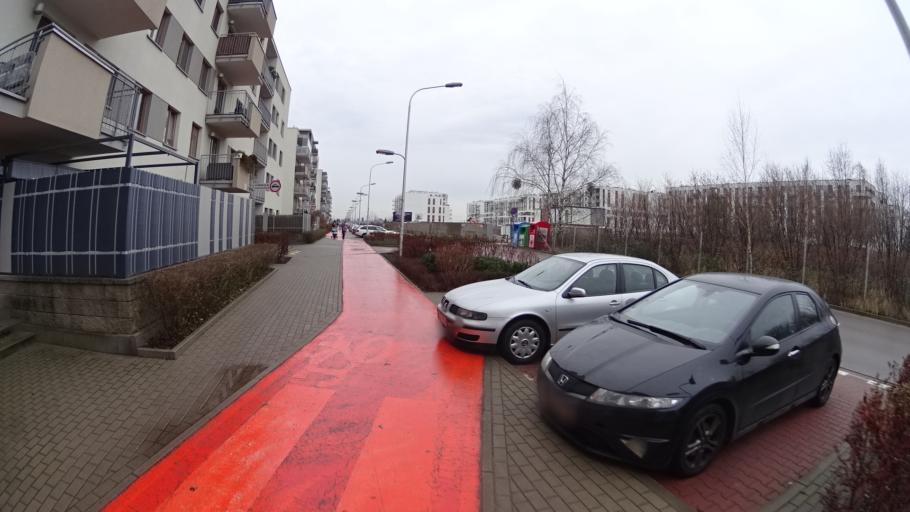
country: PL
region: Masovian Voivodeship
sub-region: Warszawa
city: Bemowo
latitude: 52.2306
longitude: 20.8911
